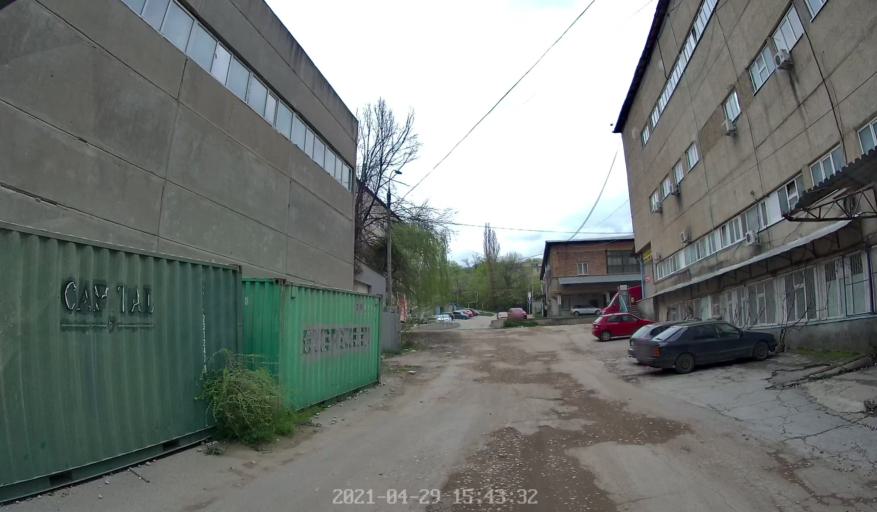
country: MD
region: Chisinau
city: Chisinau
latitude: 47.0526
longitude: 28.8114
